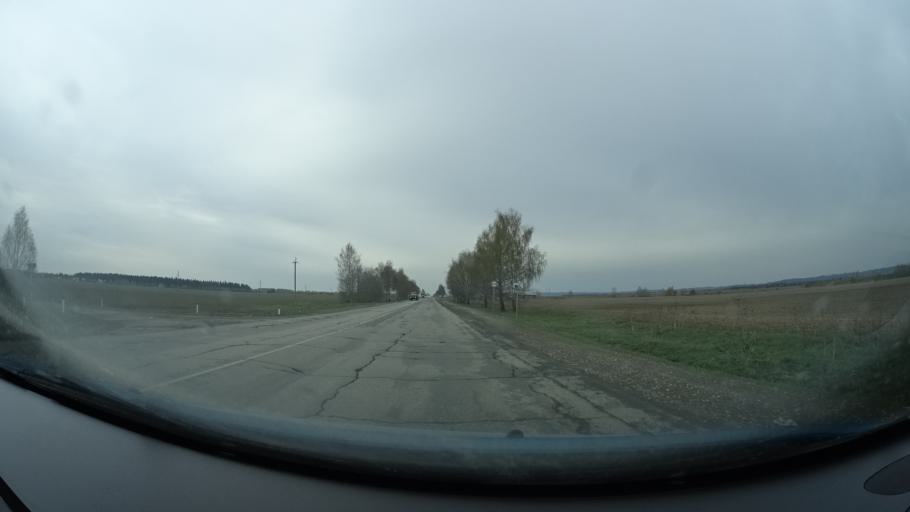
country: RU
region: Perm
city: Ust'-Kachka
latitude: 58.0727
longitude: 55.6362
